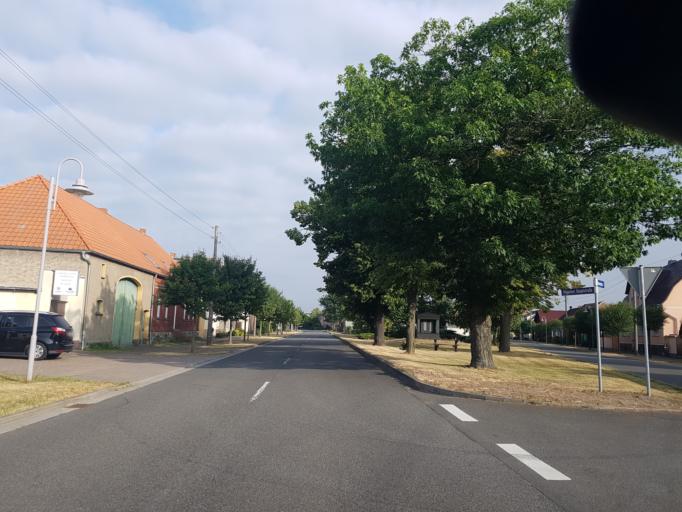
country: DE
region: Saxony-Anhalt
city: Jessen
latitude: 51.8510
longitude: 13.0323
